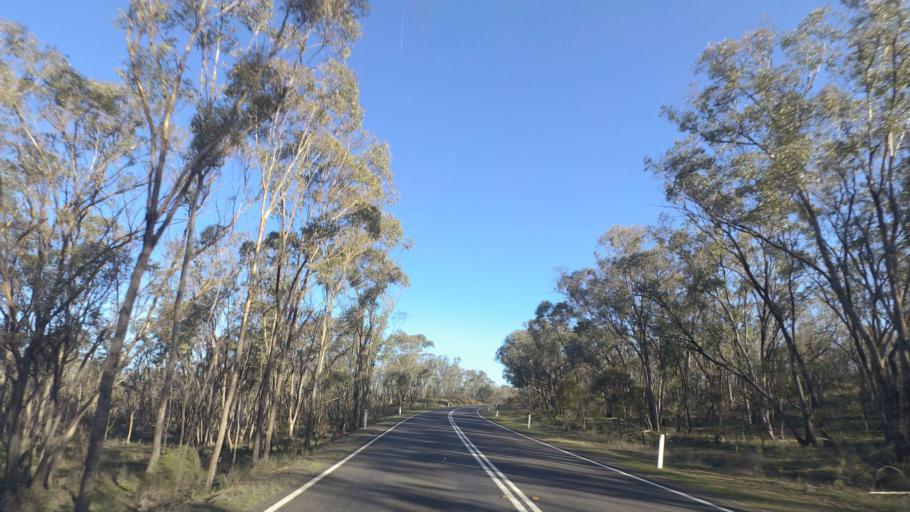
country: AU
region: Victoria
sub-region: Greater Bendigo
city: Kennington
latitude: -36.9213
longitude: 144.4911
